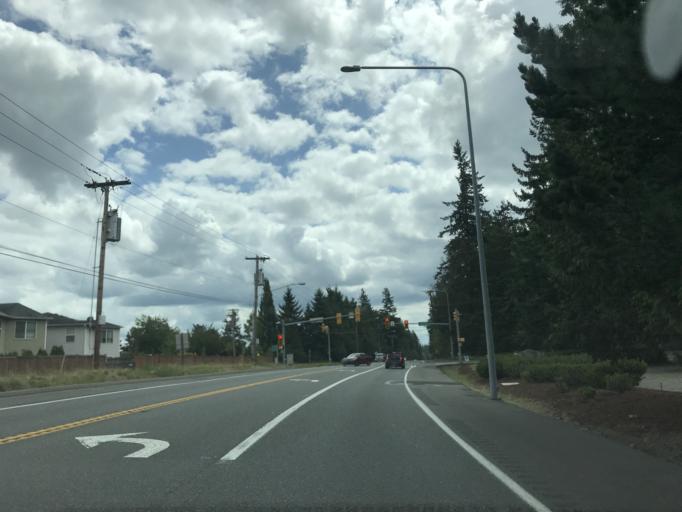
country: US
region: Washington
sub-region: King County
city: Maple Heights-Lake Desire
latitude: 47.4382
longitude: -122.1171
